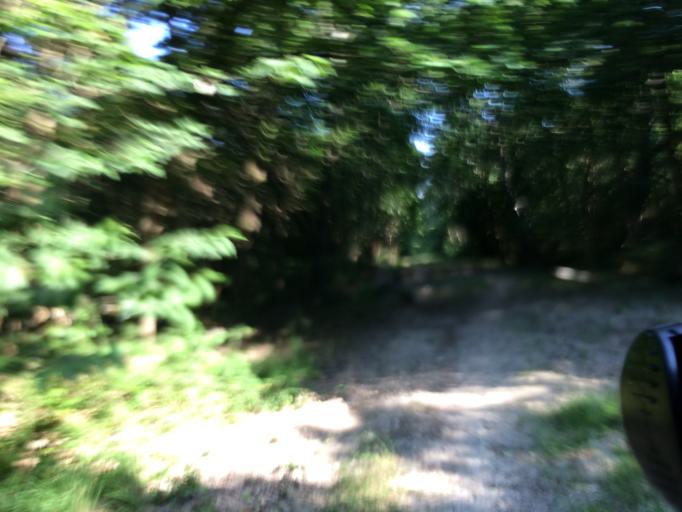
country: FR
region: Ile-de-France
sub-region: Departement de l'Essonne
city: Soisy-sur-Seine
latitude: 48.6699
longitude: 2.4574
